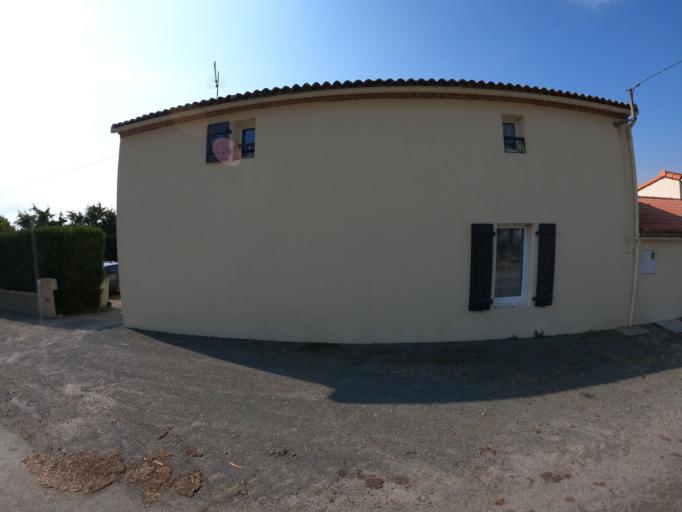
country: FR
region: Pays de la Loire
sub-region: Departement de la Vendee
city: La Bruffiere
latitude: 47.0086
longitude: -1.2073
